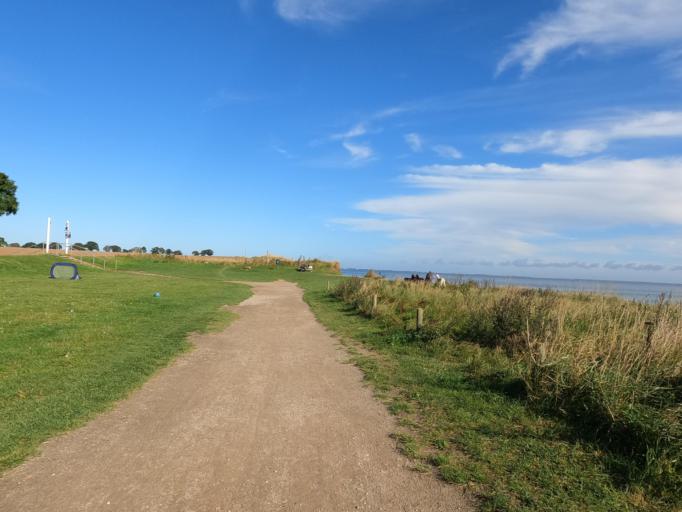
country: DE
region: Schleswig-Holstein
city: Dahme
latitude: 54.2816
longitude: 11.0827
